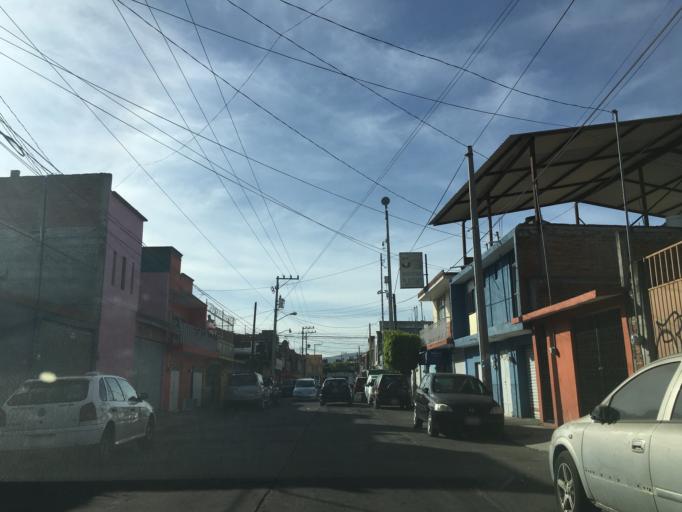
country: MX
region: Michoacan
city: Morelia
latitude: 19.7098
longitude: -101.2040
